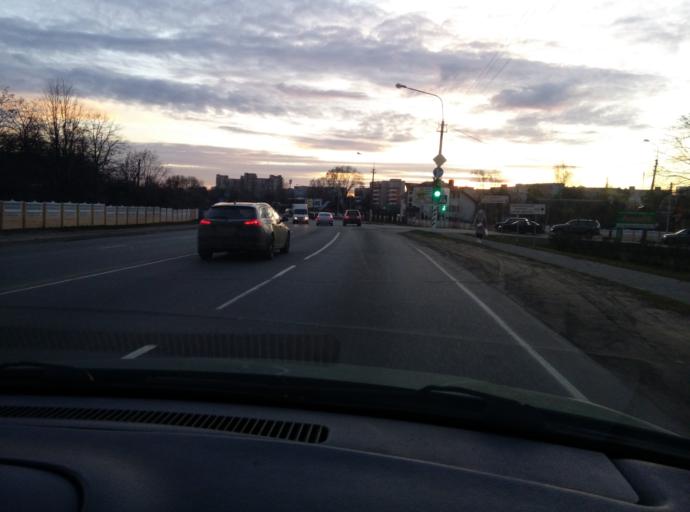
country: BY
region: Minsk
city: Horad Barysaw
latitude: 54.2268
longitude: 28.4961
